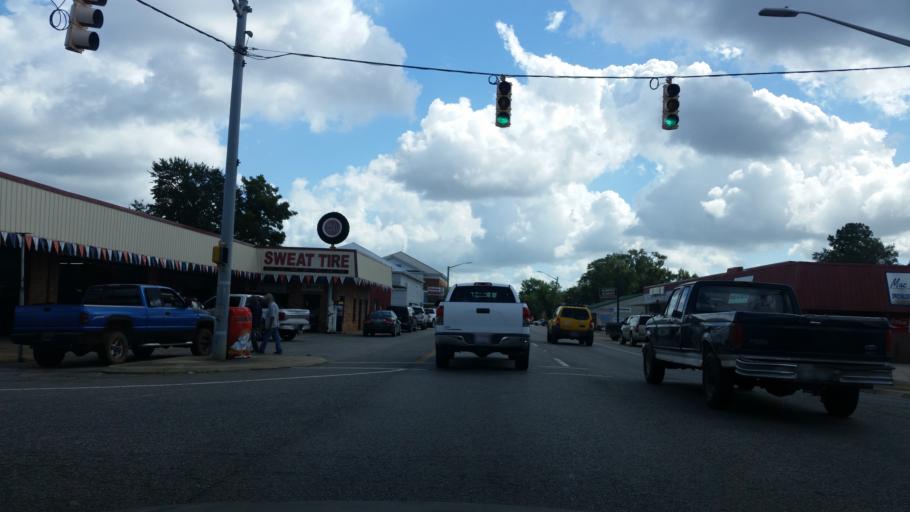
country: US
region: Alabama
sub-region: Baldwin County
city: Robertsdale
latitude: 30.5544
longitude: -87.7105
